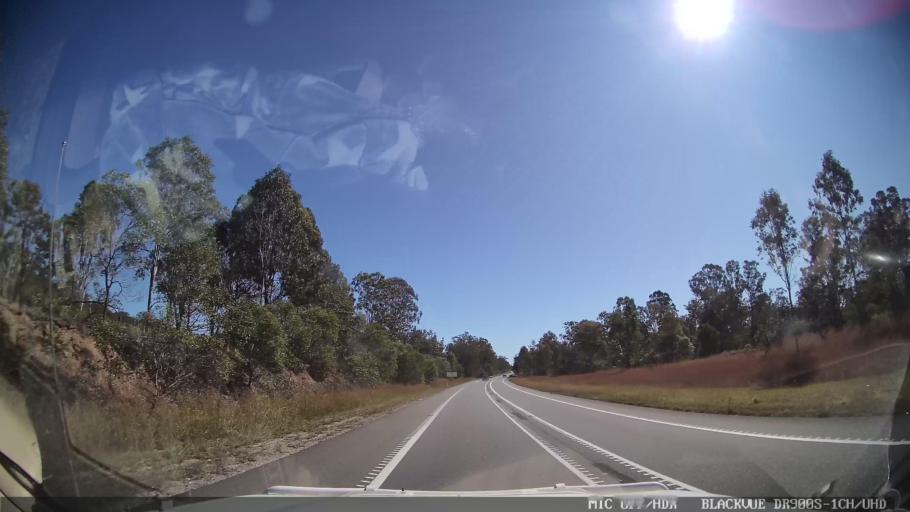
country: AU
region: Queensland
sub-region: Gympie Regional Council
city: Gympie
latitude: -26.0443
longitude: 152.5726
